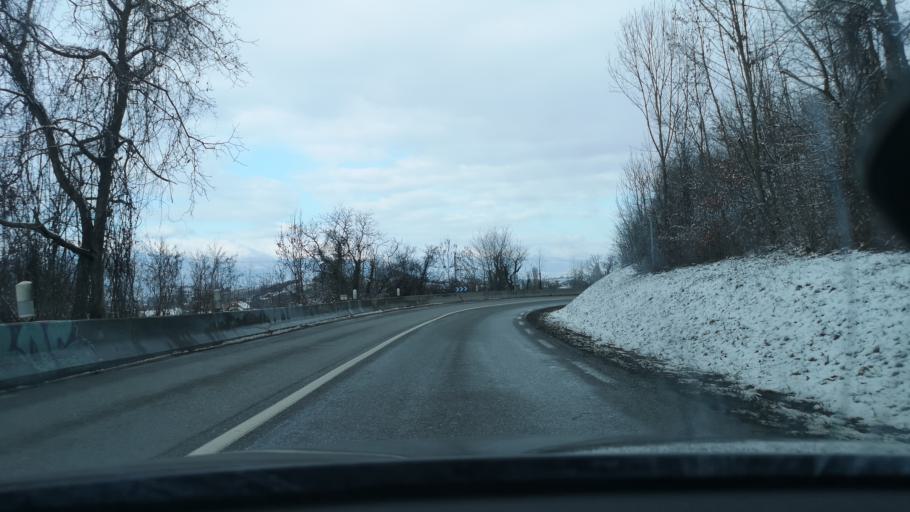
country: FR
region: Rhone-Alpes
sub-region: Departement de la Haute-Savoie
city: Saint-Julien-en-Genevois
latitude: 46.1335
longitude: 6.0582
